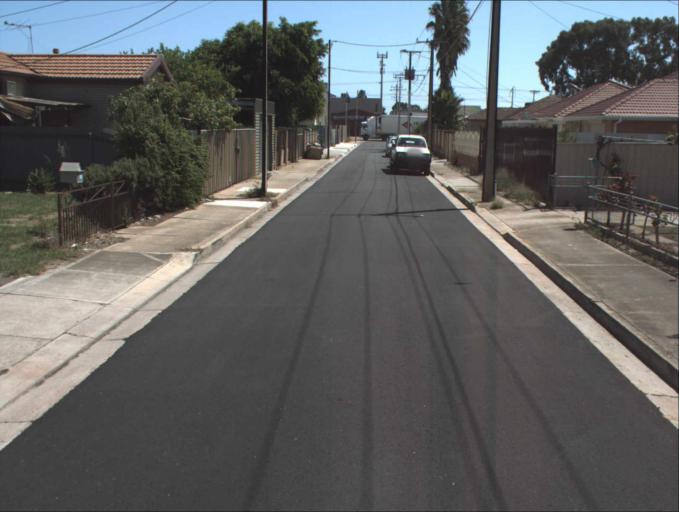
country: AU
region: South Australia
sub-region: Charles Sturt
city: Woodville North
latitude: -34.8478
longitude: 138.5481
